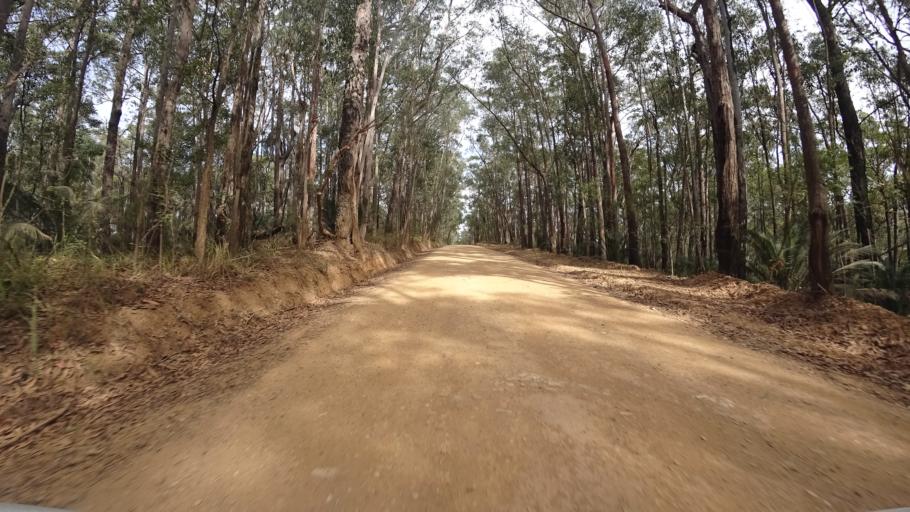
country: AU
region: New South Wales
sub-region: Shoalhaven Shire
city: Milton
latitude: -35.3756
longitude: 150.2223
